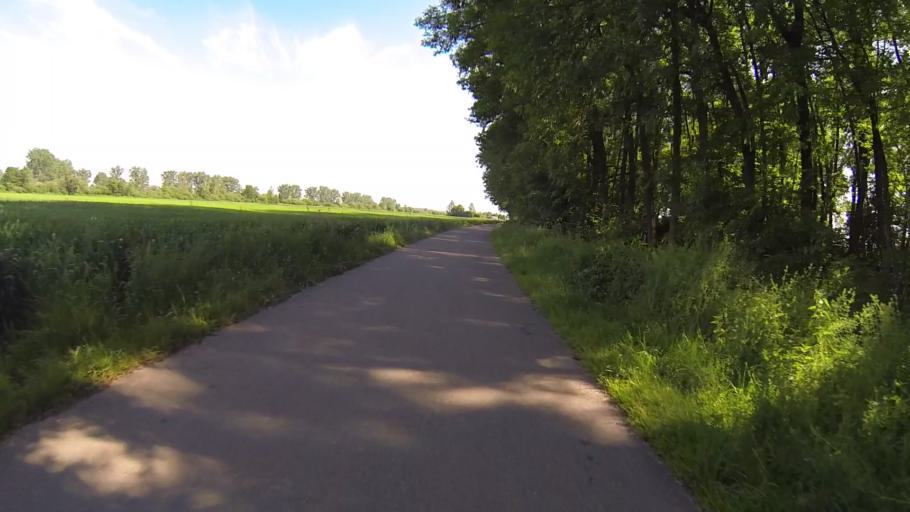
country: DE
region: Baden-Wuerttemberg
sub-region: Tuebingen Region
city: Laupheim
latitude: 48.2043
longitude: 9.8324
